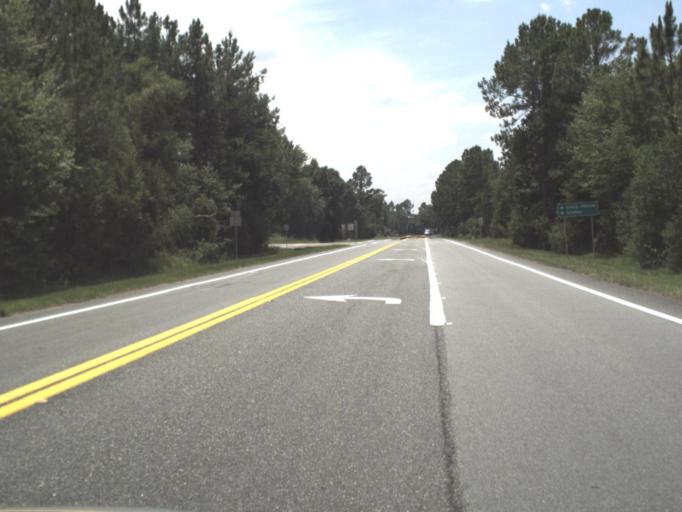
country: US
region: Florida
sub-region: Union County
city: Lake Butler
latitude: 30.0711
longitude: -82.2233
